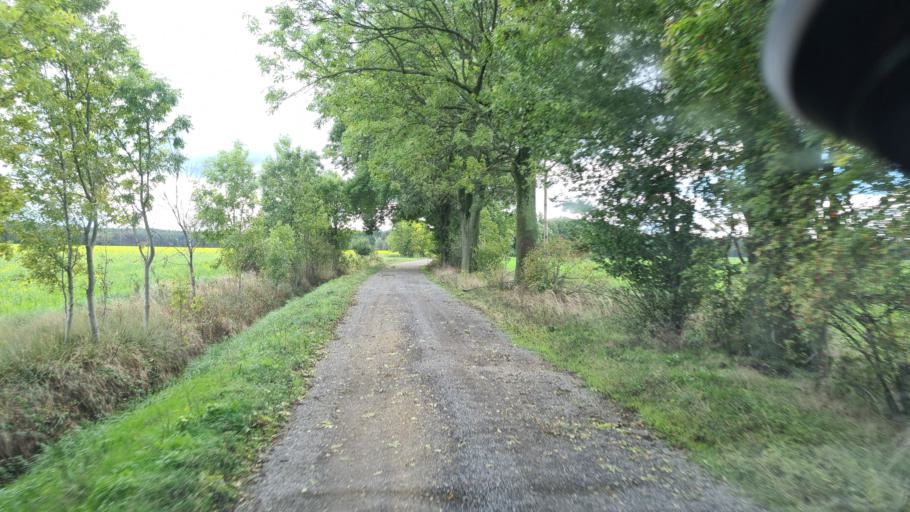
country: DE
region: Brandenburg
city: Sallgast
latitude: 51.6001
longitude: 13.8949
